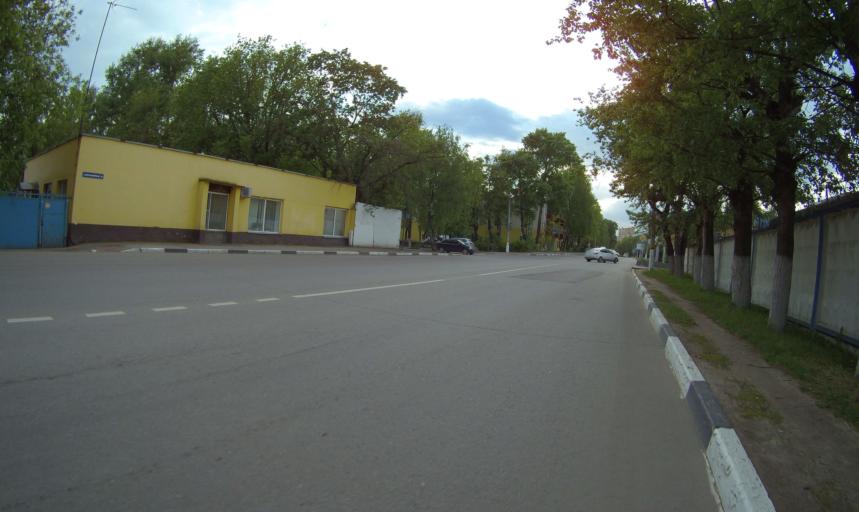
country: RU
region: Moskovskaya
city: Ramenskoye
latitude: 55.5706
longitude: 38.2473
